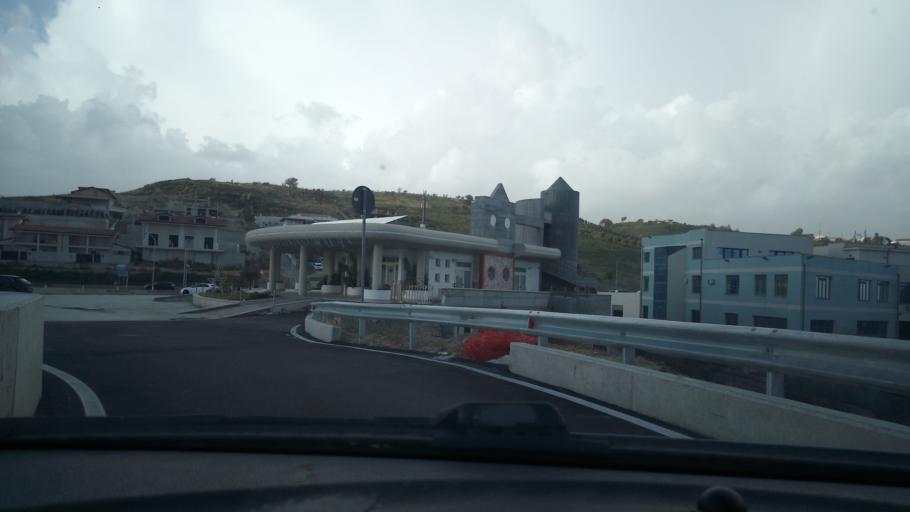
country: IT
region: Calabria
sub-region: Provincia di Catanzaro
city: Barone
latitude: 38.8347
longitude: 16.6374
